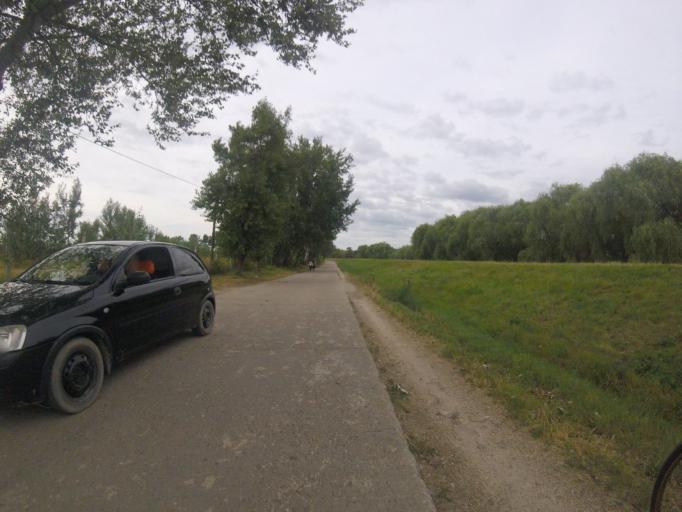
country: HU
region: Pest
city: Budakalasz
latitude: 47.6185
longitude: 19.0798
